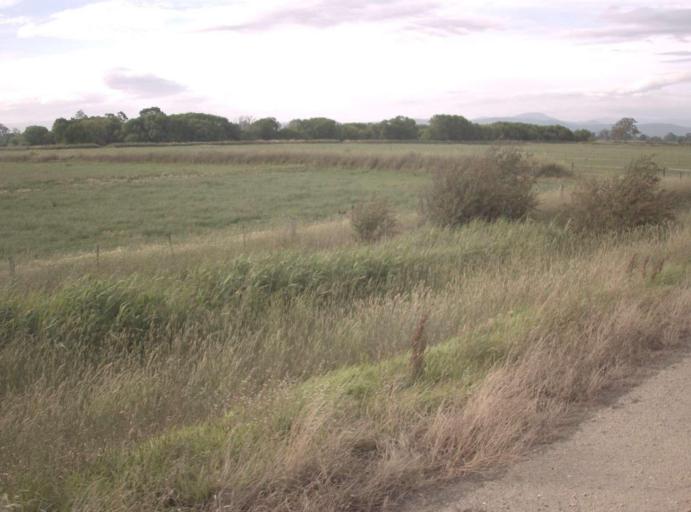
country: AU
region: Victoria
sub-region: Wellington
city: Heyfield
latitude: -37.9815
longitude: 146.8881
